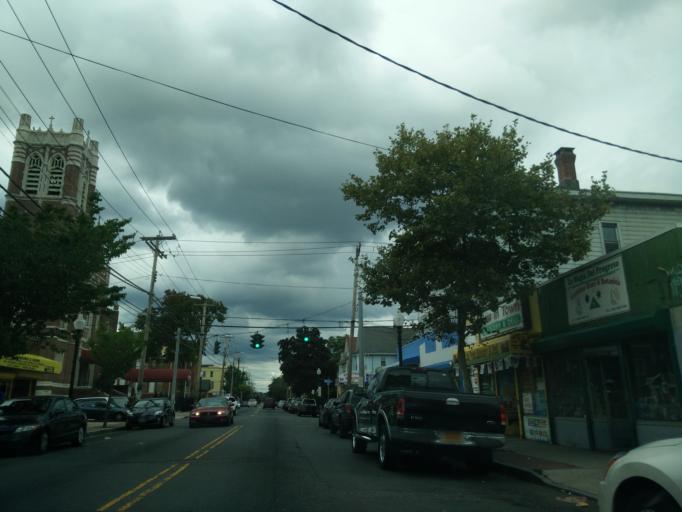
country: US
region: Connecticut
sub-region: Fairfield County
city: Bridgeport
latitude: 41.1912
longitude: -73.1804
